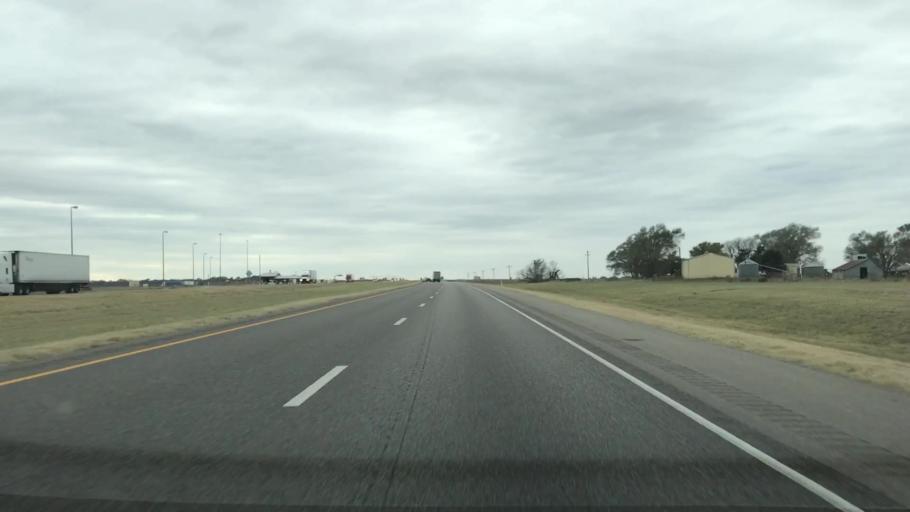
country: US
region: Oklahoma
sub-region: Beckham County
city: Erick
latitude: 35.2318
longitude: -99.9620
